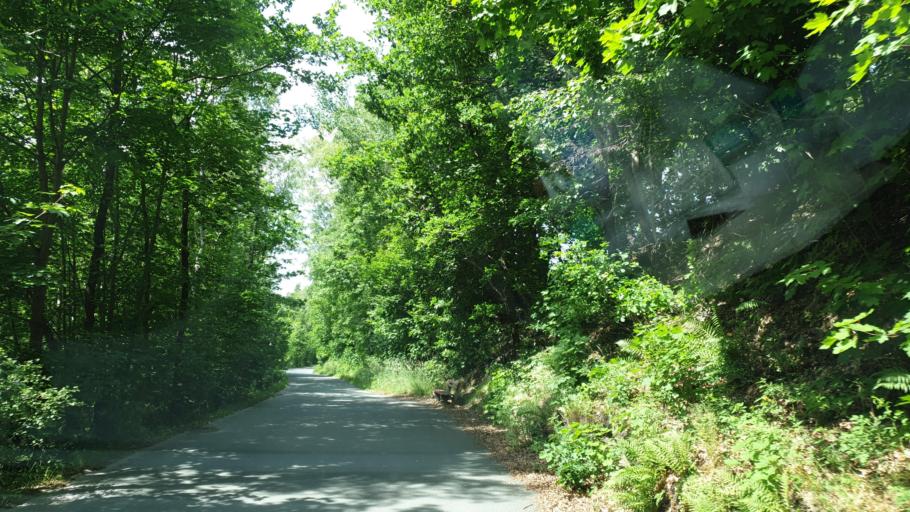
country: DE
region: Saxony
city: Adorf
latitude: 50.3278
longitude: 12.2606
